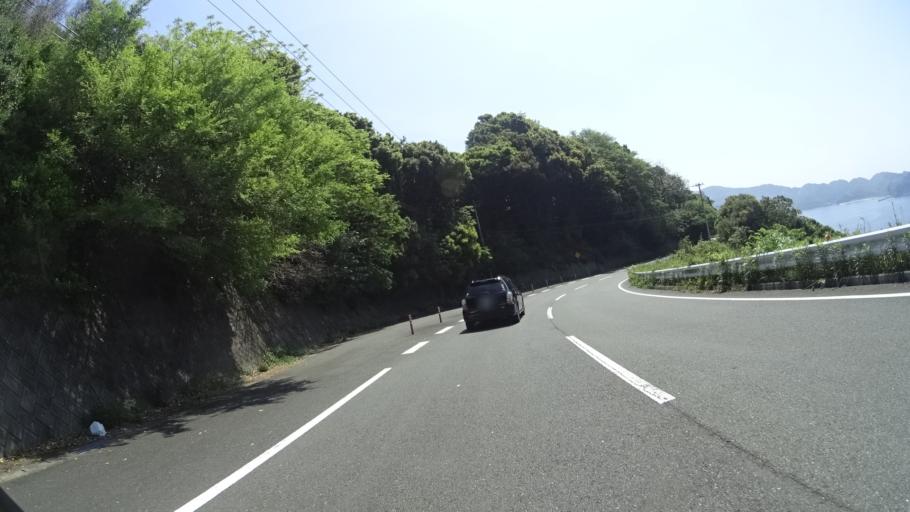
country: JP
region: Ehime
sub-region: Nishiuwa-gun
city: Ikata-cho
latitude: 33.3896
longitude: 132.0942
